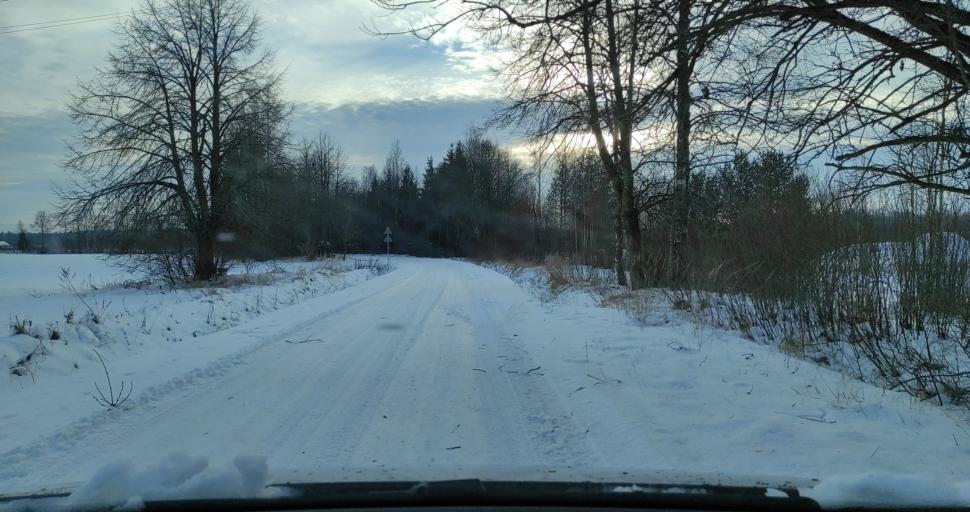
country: LV
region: Kuldigas Rajons
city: Kuldiga
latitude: 56.9416
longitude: 22.0276
